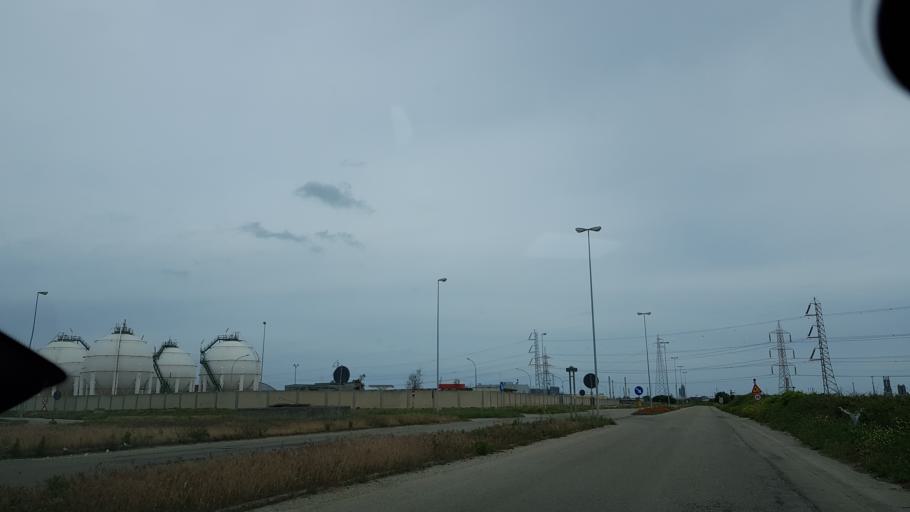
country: IT
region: Apulia
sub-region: Provincia di Brindisi
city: La Rosa
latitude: 40.6223
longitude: 17.9785
